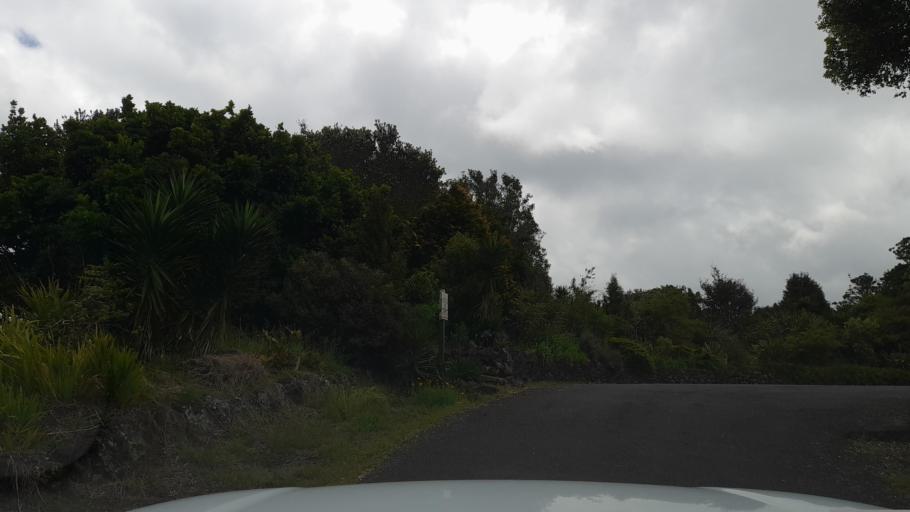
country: NZ
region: Northland
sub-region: Far North District
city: Waimate North
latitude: -35.4105
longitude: 173.7853
